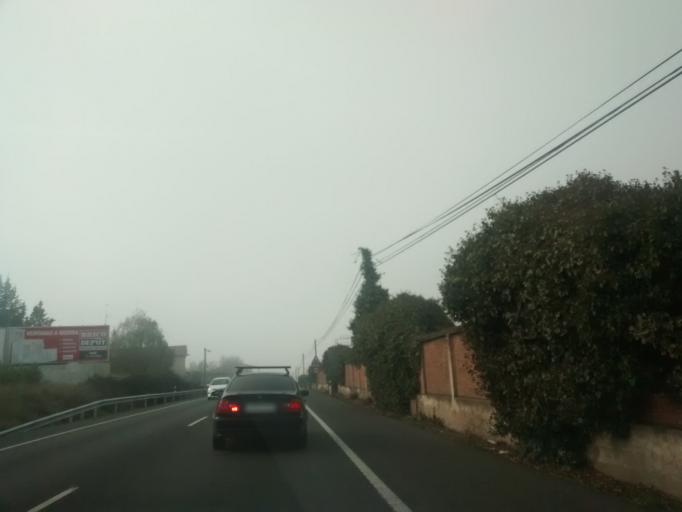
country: ES
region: La Rioja
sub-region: Provincia de La Rioja
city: Agoncillo
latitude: 42.4495
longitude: -2.3324
